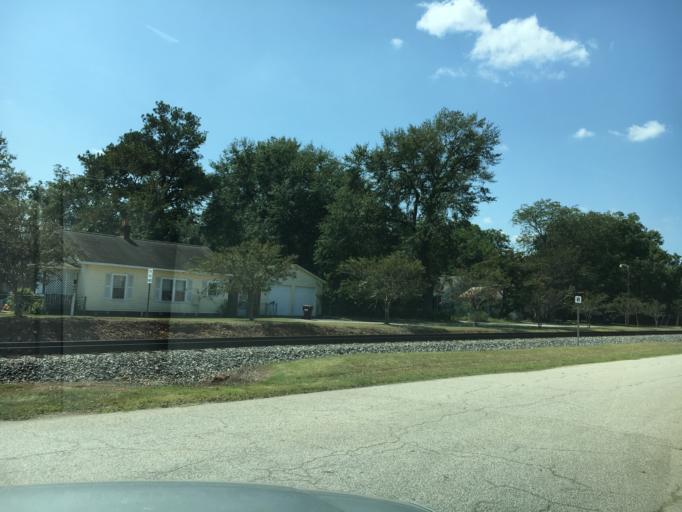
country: US
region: South Carolina
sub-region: Lexington County
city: Batesburg
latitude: 33.8449
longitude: -81.6582
